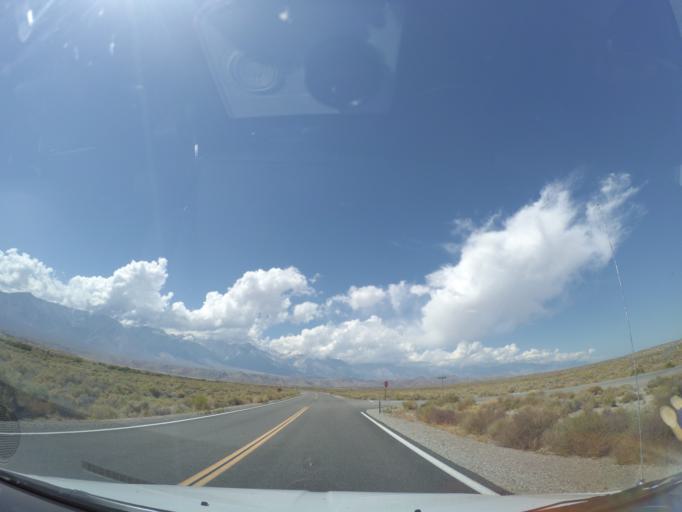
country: US
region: California
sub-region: Inyo County
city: Lone Pine
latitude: 36.5739
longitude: -117.9964
